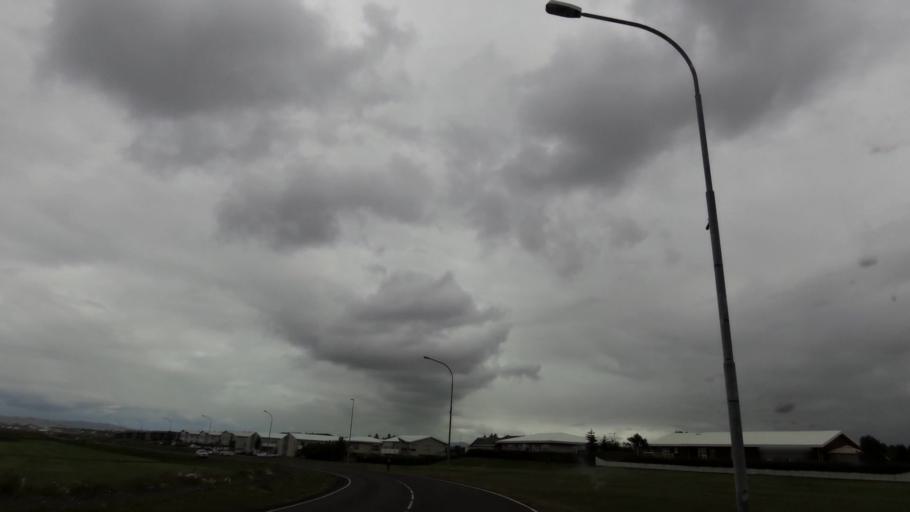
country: IS
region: Capital Region
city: Alftanes
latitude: 64.1000
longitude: -22.0248
